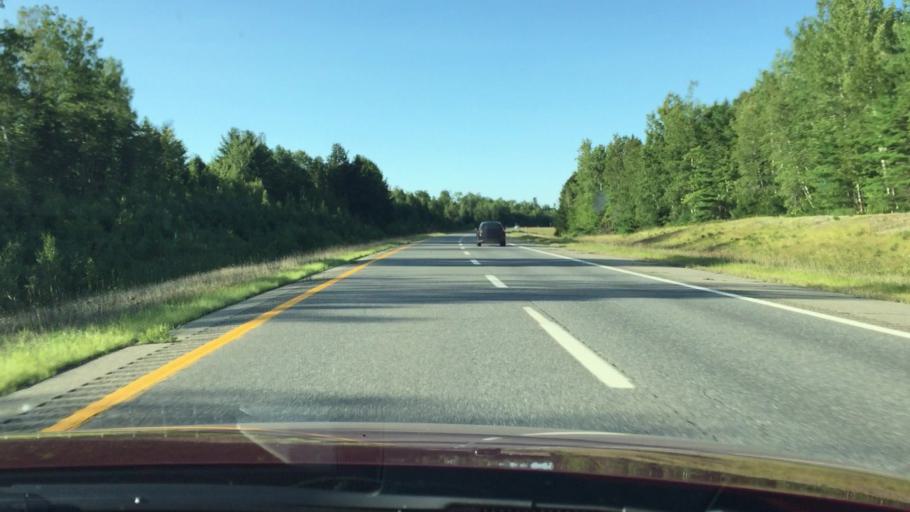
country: US
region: Maine
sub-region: Penobscot County
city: Lincoln
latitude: 45.4500
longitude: -68.5908
